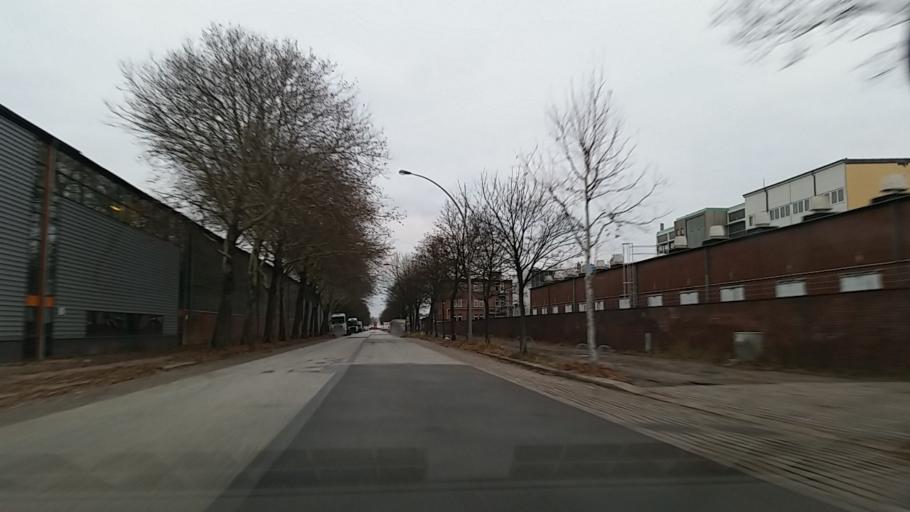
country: DE
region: Hamburg
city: Wandsbek
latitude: 53.5347
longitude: 10.0940
